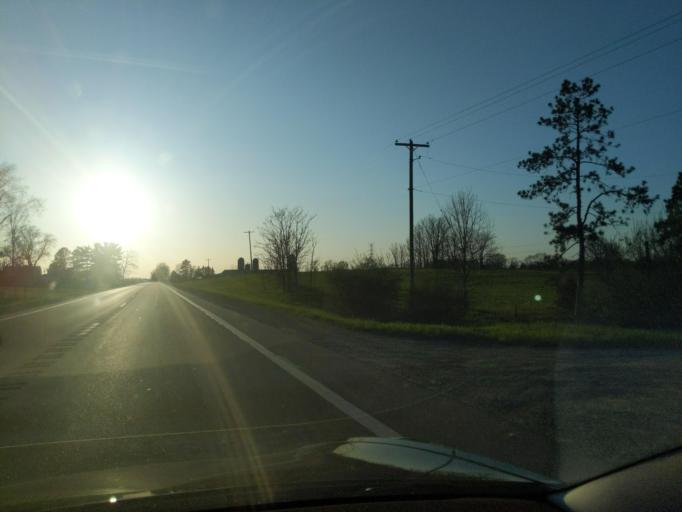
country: US
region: Michigan
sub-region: Ingham County
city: Stockbridge
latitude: 42.4163
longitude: -84.1446
